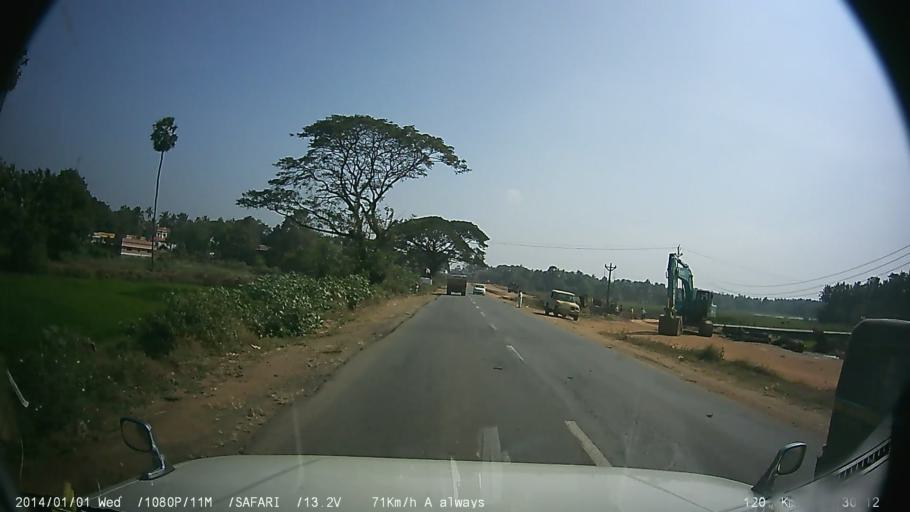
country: IN
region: Kerala
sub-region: Palakkad district
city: Palakkad
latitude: 10.6443
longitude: 76.5409
